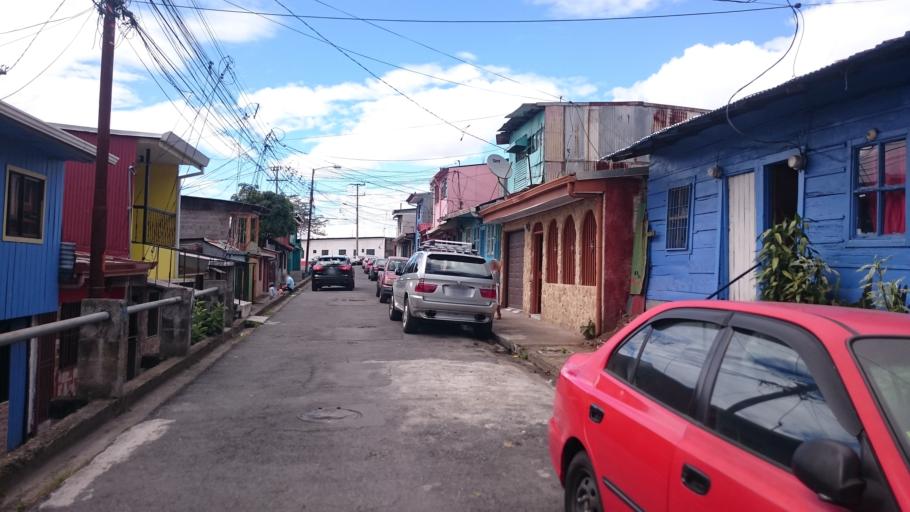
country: CR
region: San Jose
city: Calle Blancos
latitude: 9.9439
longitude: -84.0709
